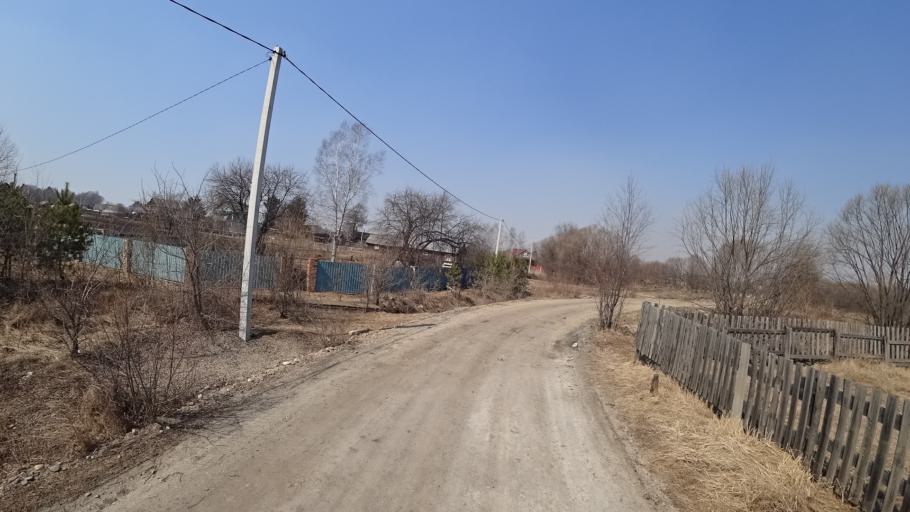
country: RU
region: Amur
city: Novobureyskiy
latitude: 49.7763
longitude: 129.8488
